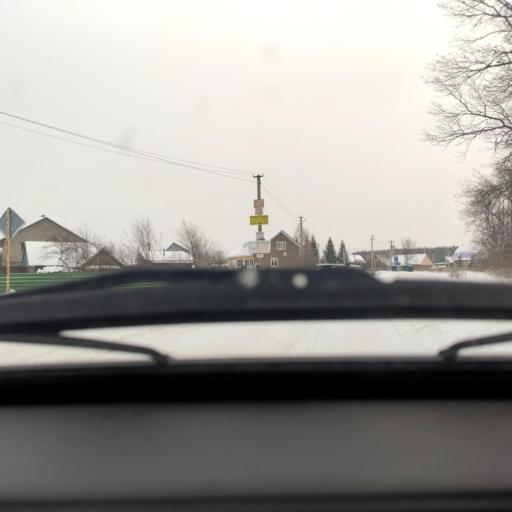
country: RU
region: Bashkortostan
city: Mikhaylovka
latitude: 54.8539
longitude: 55.8772
